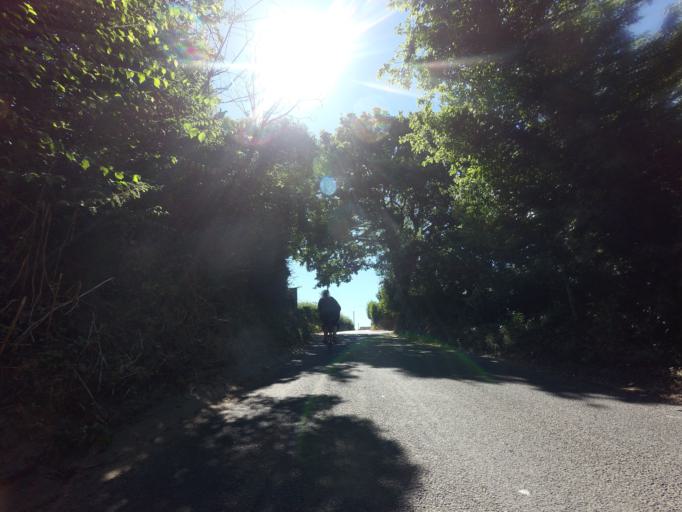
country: GB
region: England
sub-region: Kent
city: Eastry
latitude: 51.2666
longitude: 1.3037
